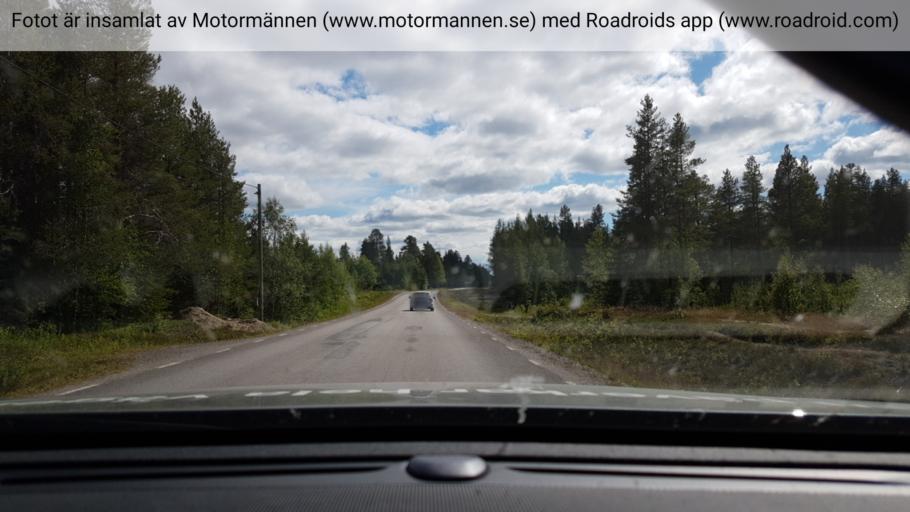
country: SE
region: Vaesterbotten
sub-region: Sorsele Kommun
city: Sorsele
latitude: 65.5686
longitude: 17.5238
